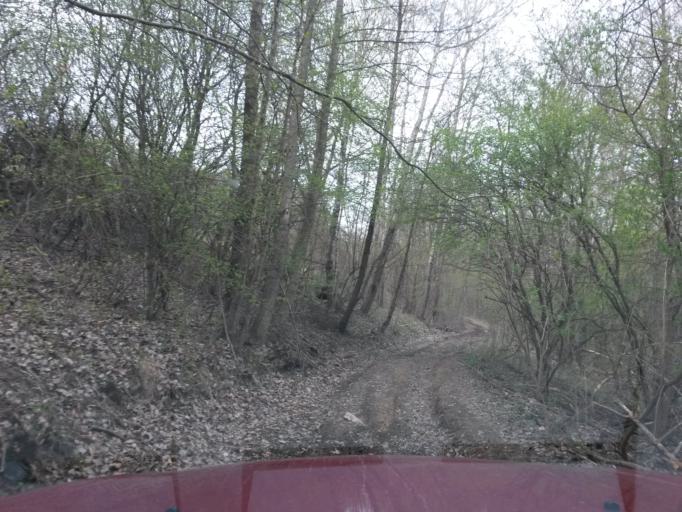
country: SK
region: Kosicky
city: Kosice
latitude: 48.7410
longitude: 21.1180
